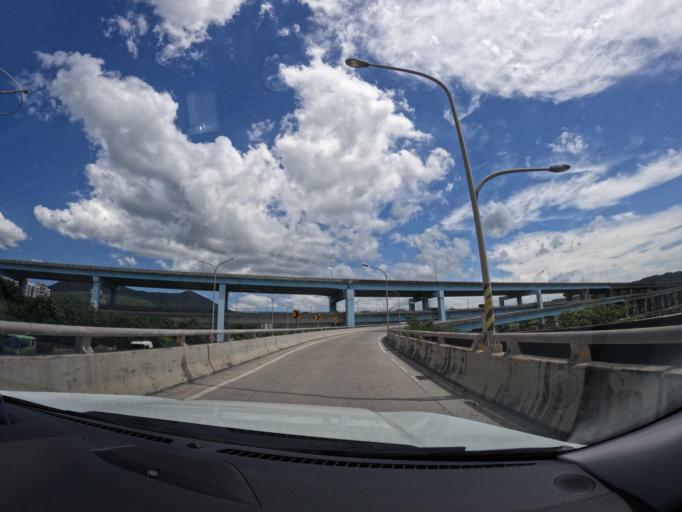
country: TW
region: Taipei
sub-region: Taipei
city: Banqiao
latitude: 25.1489
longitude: 121.3895
